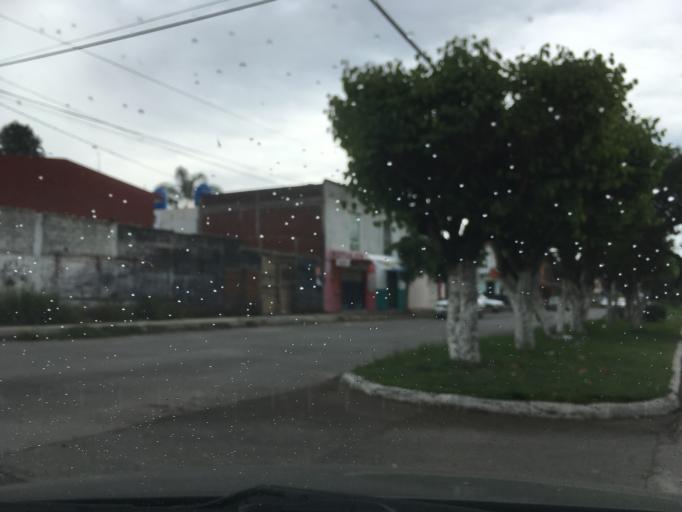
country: MX
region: Michoacan
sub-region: Uruapan
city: Uruapan
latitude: 19.4076
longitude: -102.0474
